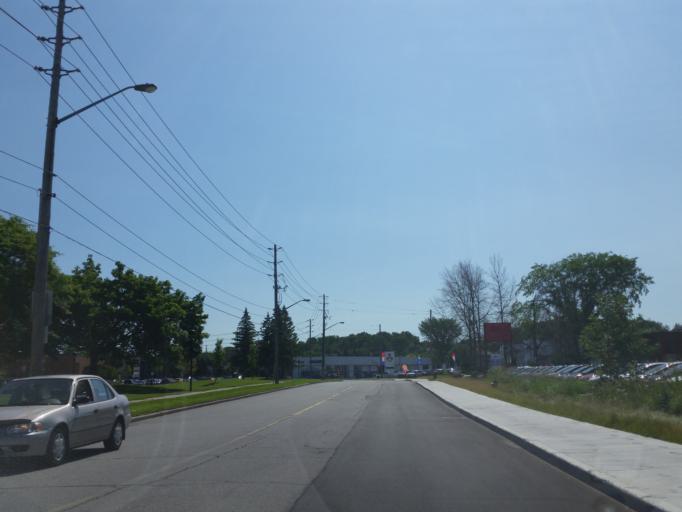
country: CA
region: Quebec
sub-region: Outaouais
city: Gatineau
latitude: 45.4656
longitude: -75.5458
